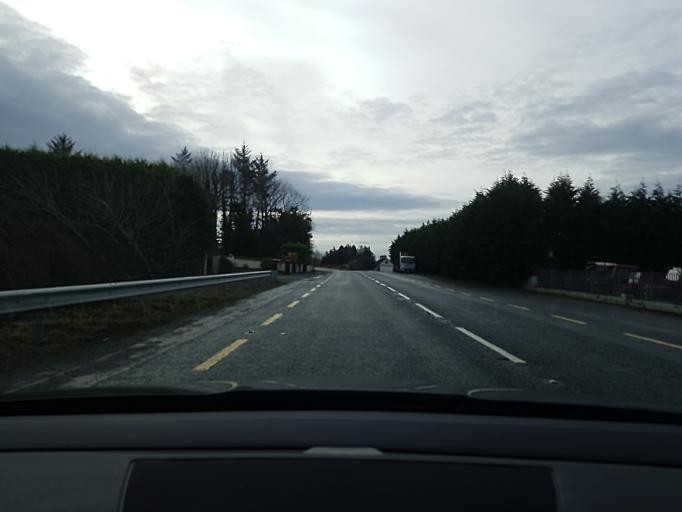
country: IE
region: Connaught
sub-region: Maigh Eo
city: Castlebar
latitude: 53.8068
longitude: -9.3165
